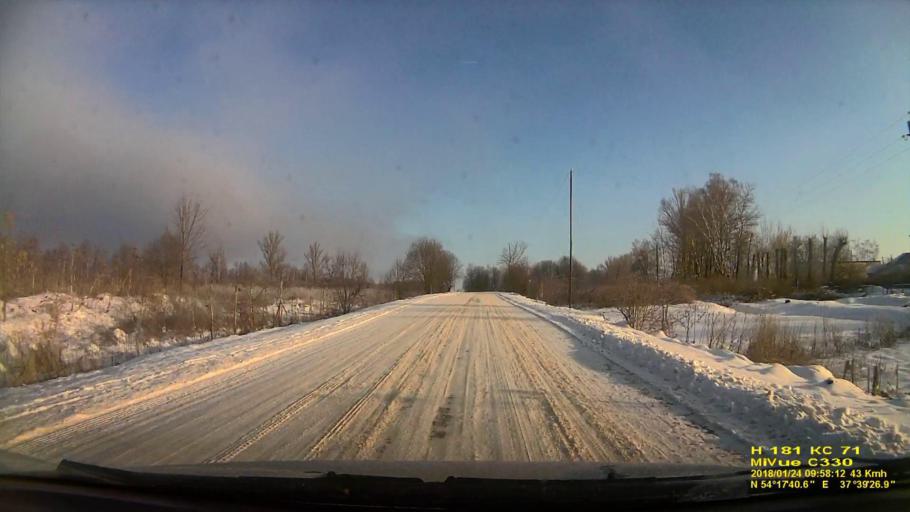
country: RU
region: Tula
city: Gorelki
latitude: 54.2947
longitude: 37.6575
